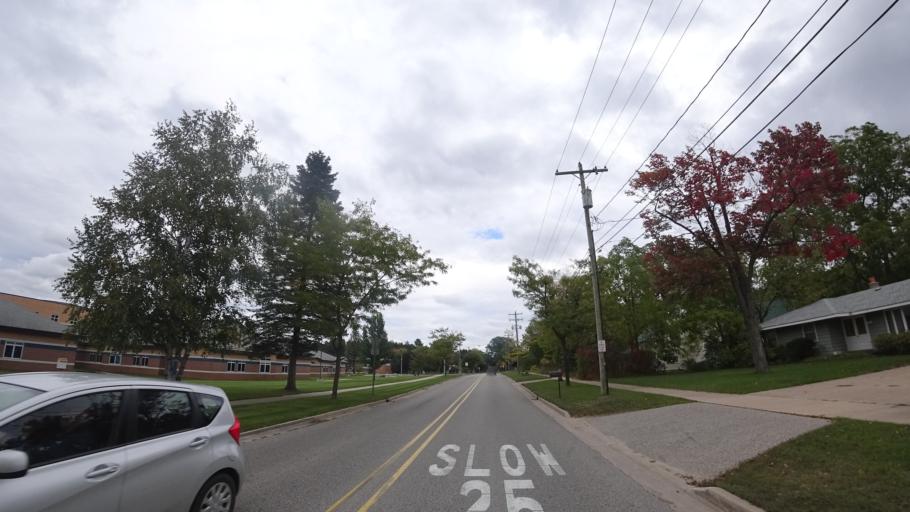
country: US
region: Michigan
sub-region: Emmet County
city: Harbor Springs
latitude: 45.4353
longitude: -84.9902
